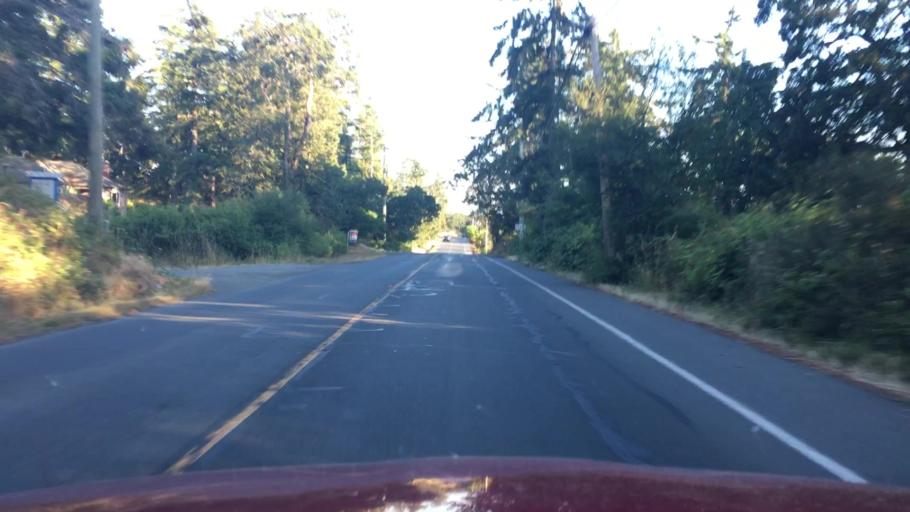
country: CA
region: British Columbia
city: Victoria
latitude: 48.4868
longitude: -123.3555
